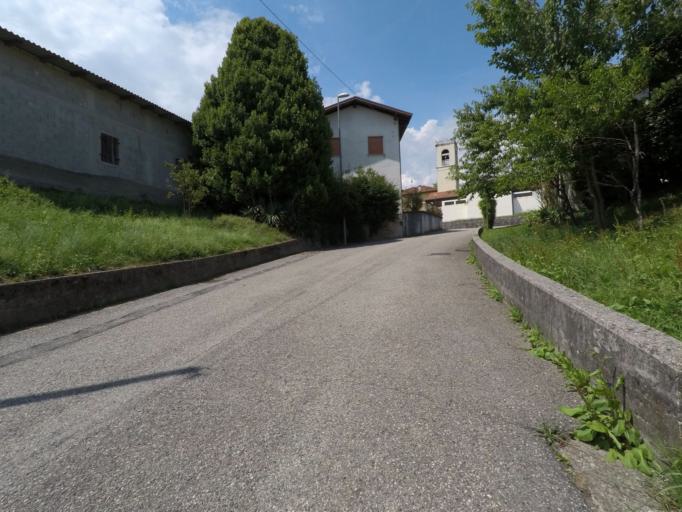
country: IT
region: Friuli Venezia Giulia
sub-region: Provincia di Pordenone
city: Lestans
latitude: 46.1785
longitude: 12.8935
